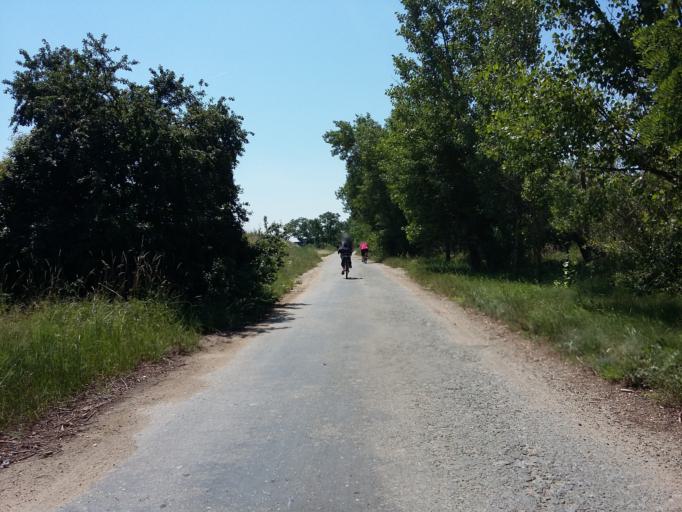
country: AT
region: Lower Austria
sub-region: Politischer Bezirk Ganserndorf
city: Marchegg
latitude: 48.2931
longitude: 16.9680
